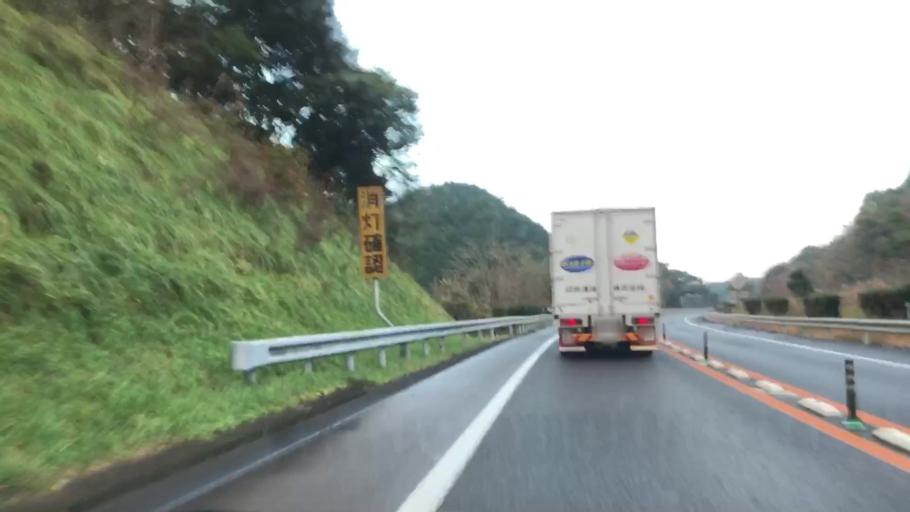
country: JP
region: Saga Prefecture
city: Ureshinomachi-shimojuku
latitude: 33.1561
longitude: 129.9033
